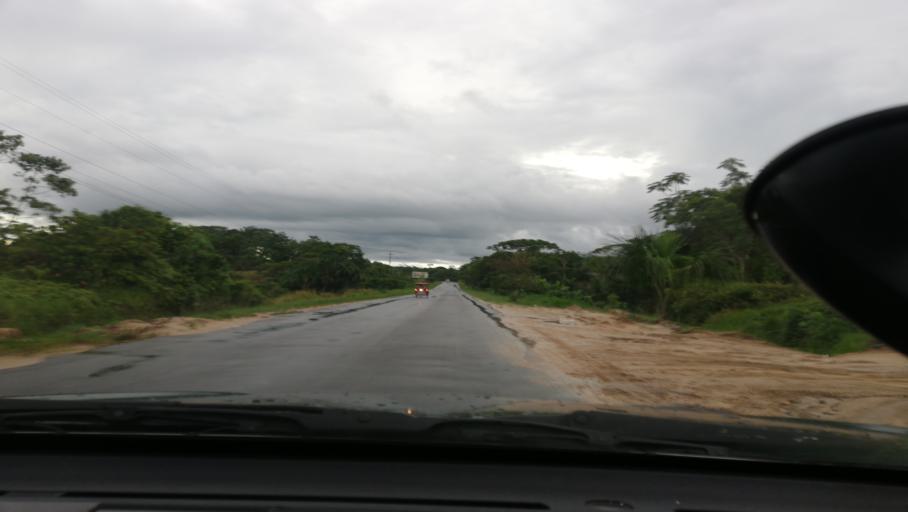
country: PE
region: Loreto
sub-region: Provincia de Maynas
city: Iquitos
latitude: -3.9090
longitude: -73.3615
